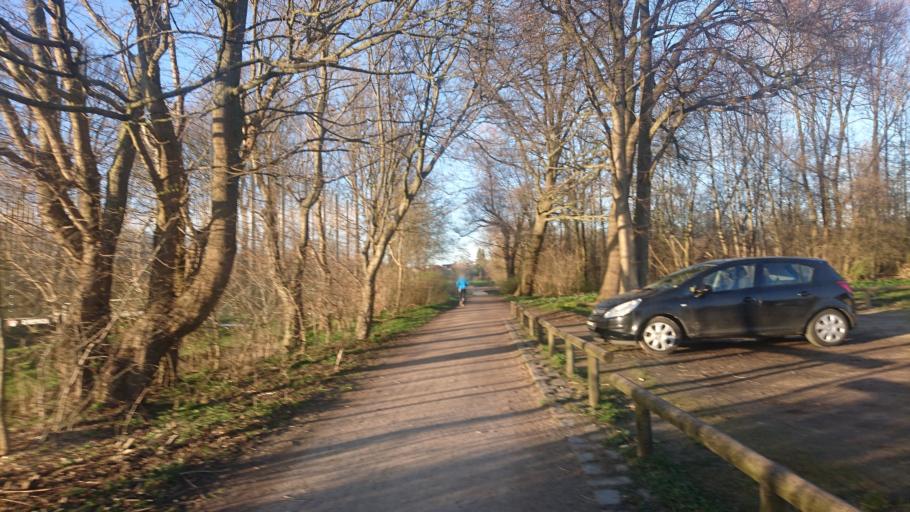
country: DK
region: Capital Region
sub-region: Lyngby-Tarbaek Kommune
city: Kongens Lyngby
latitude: 55.7452
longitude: 12.5175
